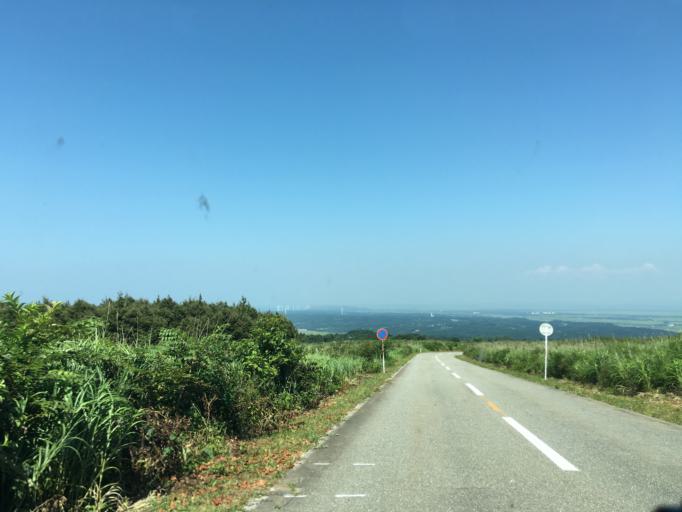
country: JP
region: Akita
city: Tenno
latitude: 39.9396
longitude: 139.8657
